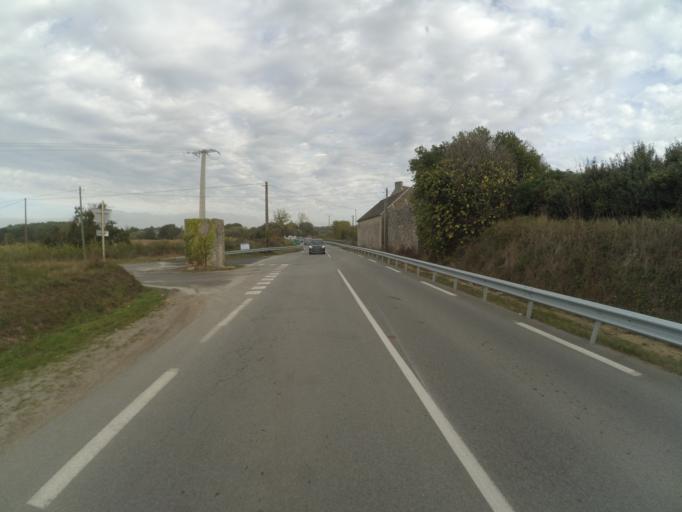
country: FR
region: Brittany
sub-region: Departement du Morbihan
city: Sainte-Helene
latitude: 47.6946
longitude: -3.2162
